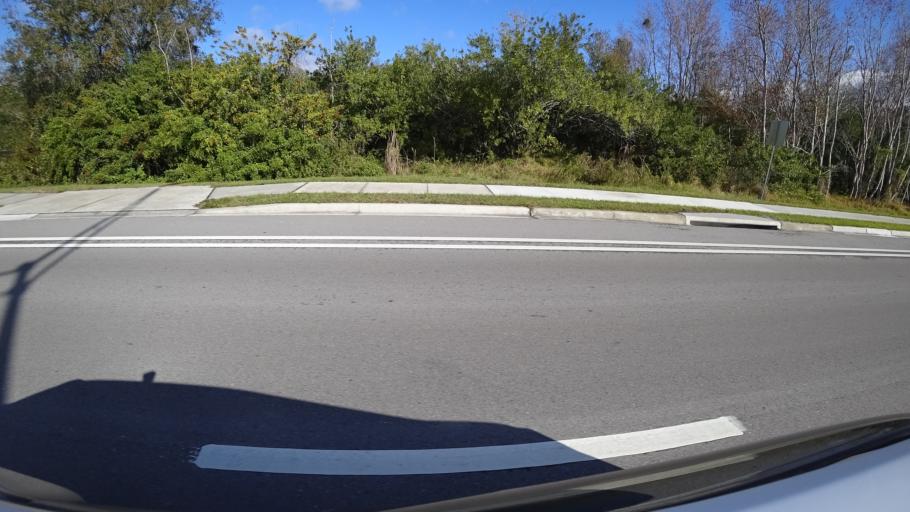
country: US
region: Florida
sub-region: Manatee County
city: Samoset
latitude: 27.4619
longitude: -82.5071
